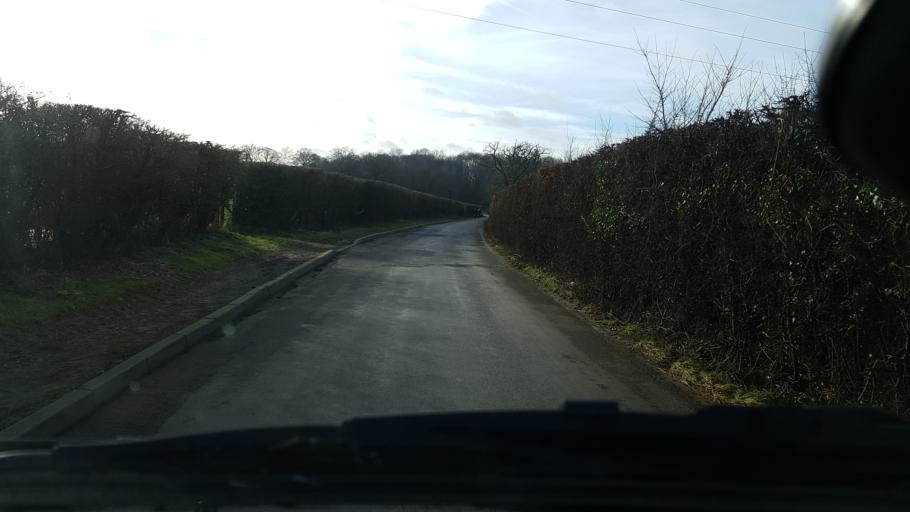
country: GB
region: England
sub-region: Surrey
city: Cobham
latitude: 51.3166
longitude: -0.4183
